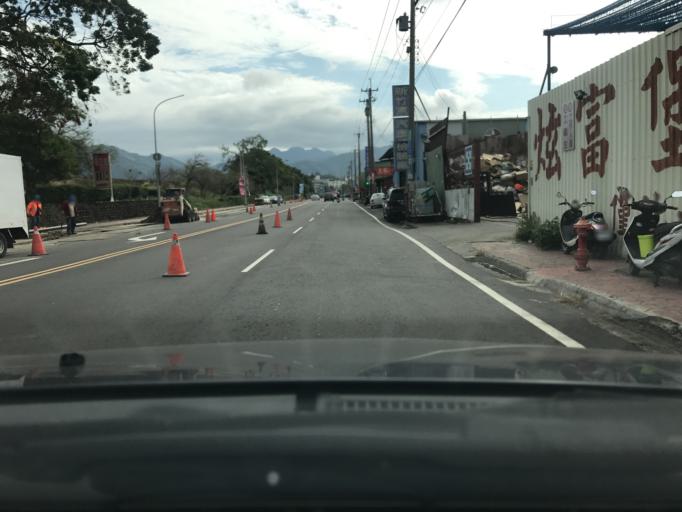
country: TW
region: Taiwan
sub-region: Hsinchu
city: Zhubei
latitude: 24.7302
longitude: 121.0997
